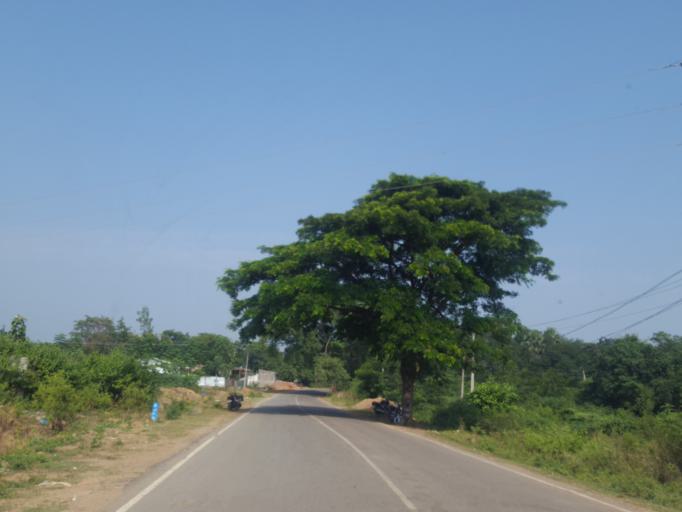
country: IN
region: Telangana
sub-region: Khammam
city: Yellandu
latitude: 17.6069
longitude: 80.3153
